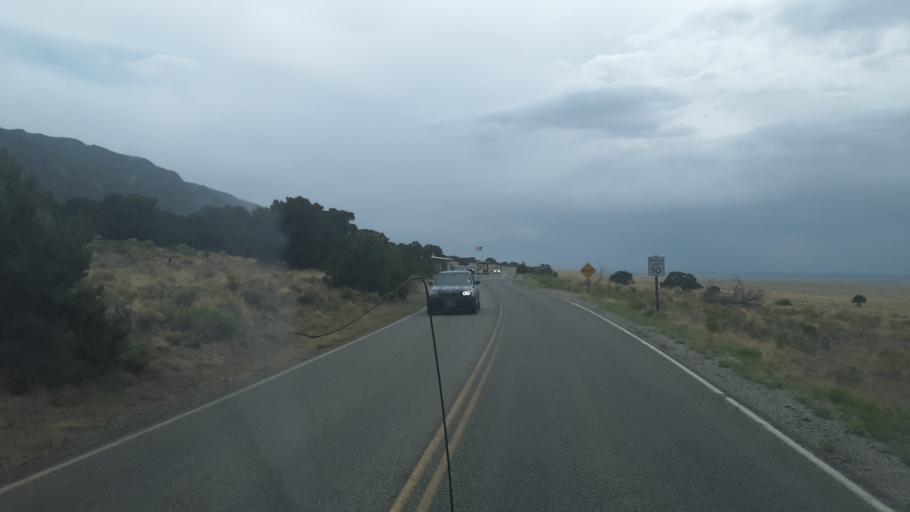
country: US
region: Colorado
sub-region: Alamosa County
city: Alamosa East
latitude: 37.7264
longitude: -105.5183
